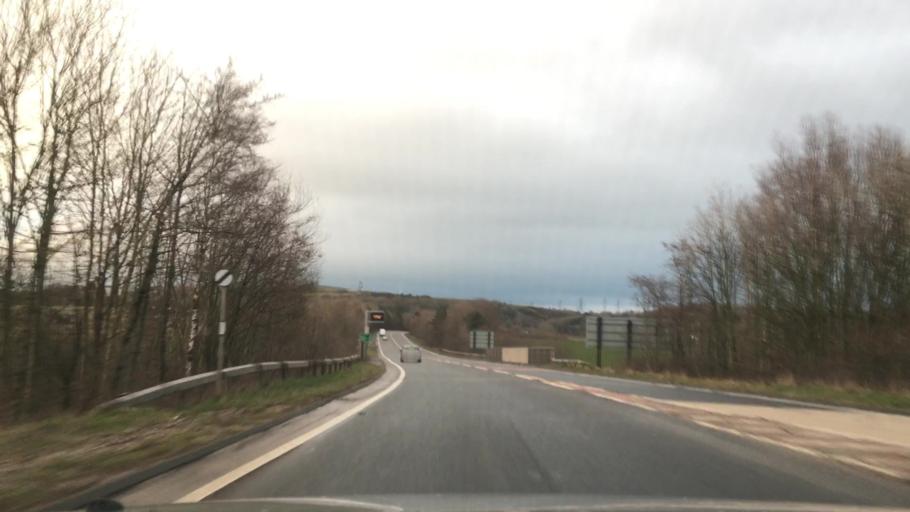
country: GB
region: England
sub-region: Cumbria
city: Askam in Furness
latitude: 54.1571
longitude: -3.2097
